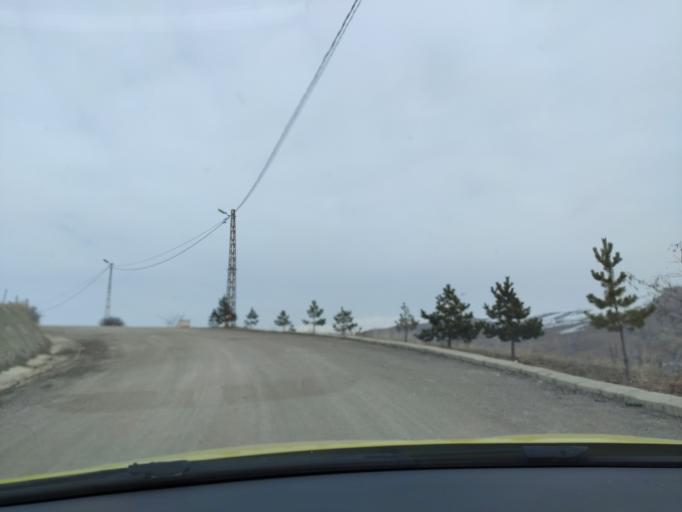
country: TR
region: Bayburt
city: Bayburt
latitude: 40.2608
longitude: 40.2206
